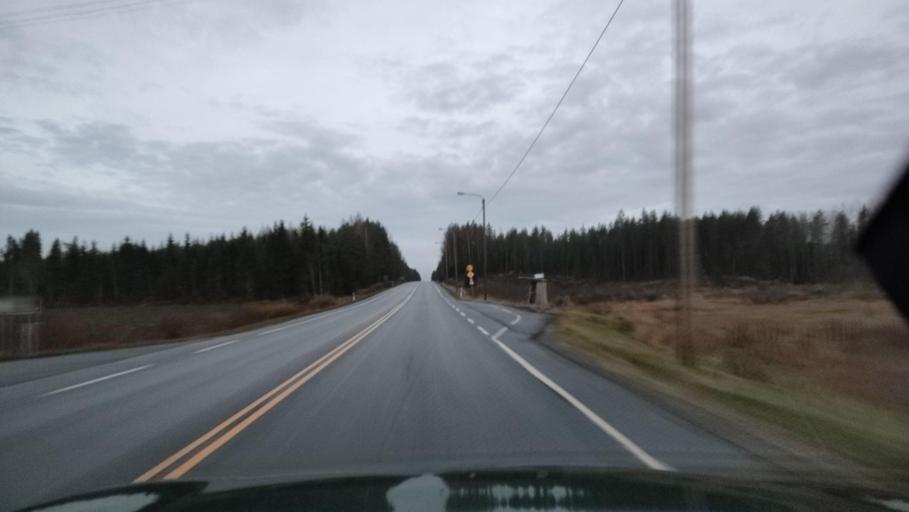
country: FI
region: Ostrobothnia
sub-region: Vaasa
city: Ristinummi
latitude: 62.9706
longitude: 21.7677
